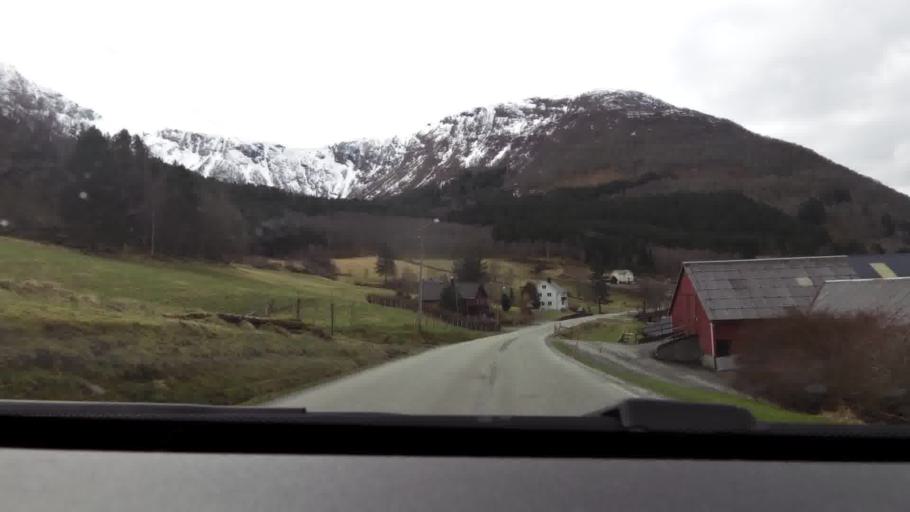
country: NO
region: More og Romsdal
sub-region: Gjemnes
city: Batnfjordsora
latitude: 62.9262
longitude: 7.5964
